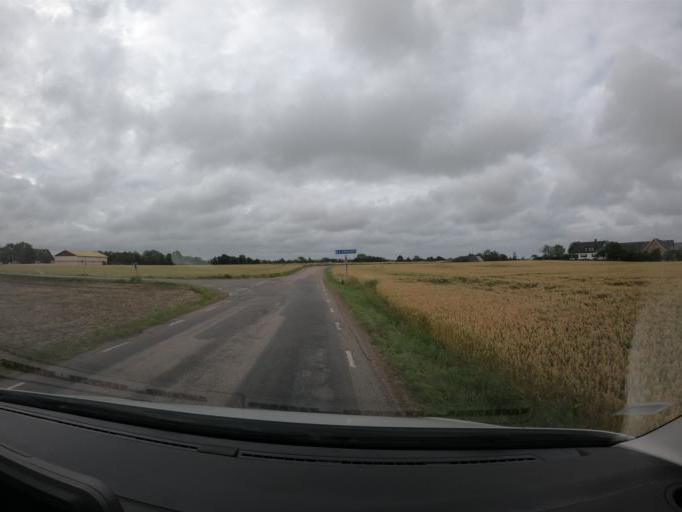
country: SE
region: Skane
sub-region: Bastads Kommun
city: Forslov
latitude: 56.3548
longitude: 12.7829
